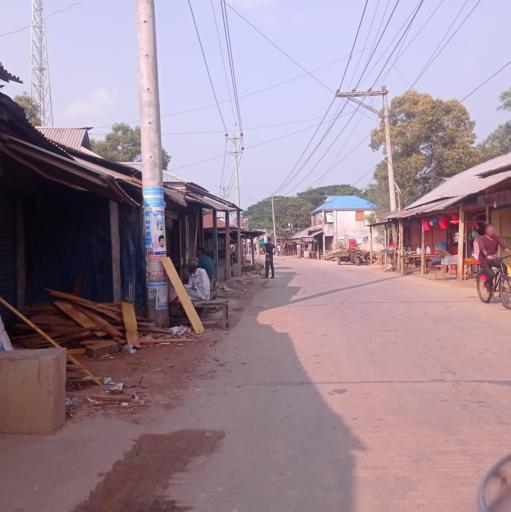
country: BD
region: Dhaka
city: Bhairab Bazar
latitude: 24.0624
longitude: 90.8410
